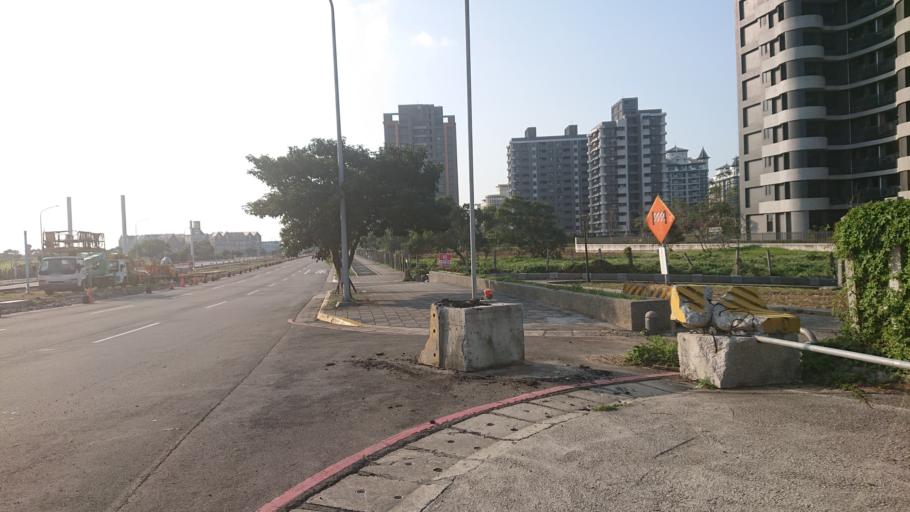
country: TW
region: Taipei
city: Taipei
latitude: 25.1908
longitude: 121.4302
